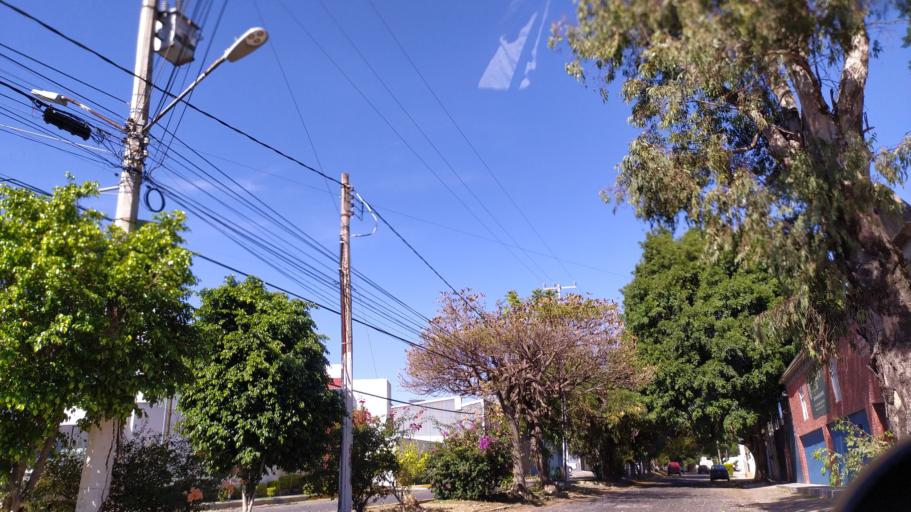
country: MX
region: Jalisco
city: Guadalajara
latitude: 20.6803
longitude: -103.4482
